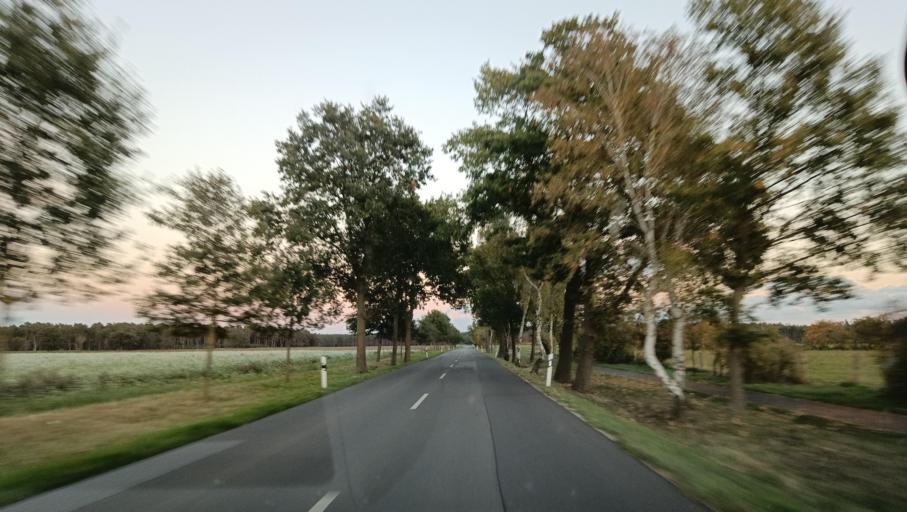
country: DE
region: Mecklenburg-Vorpommern
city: Ludwigslust
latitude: 53.2774
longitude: 11.5053
